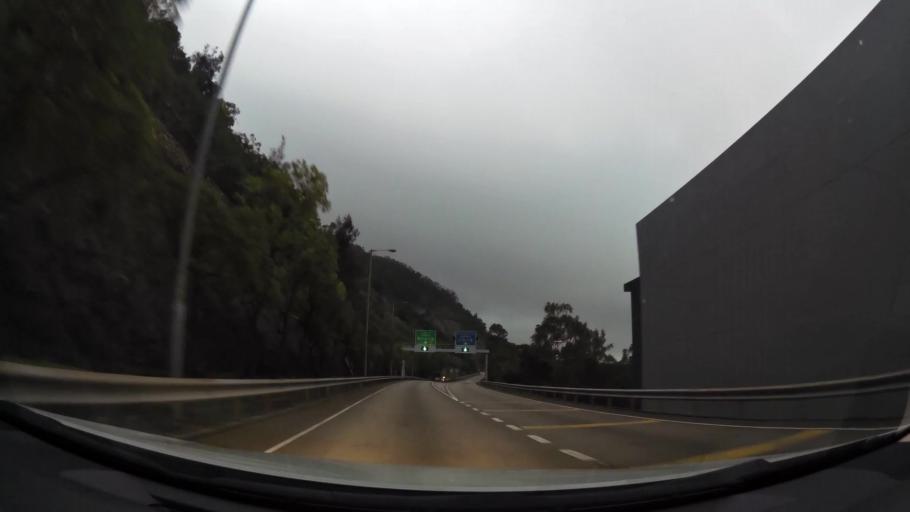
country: HK
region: Tsuen Wan
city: Tsuen Wan
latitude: 22.3545
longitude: 114.0860
